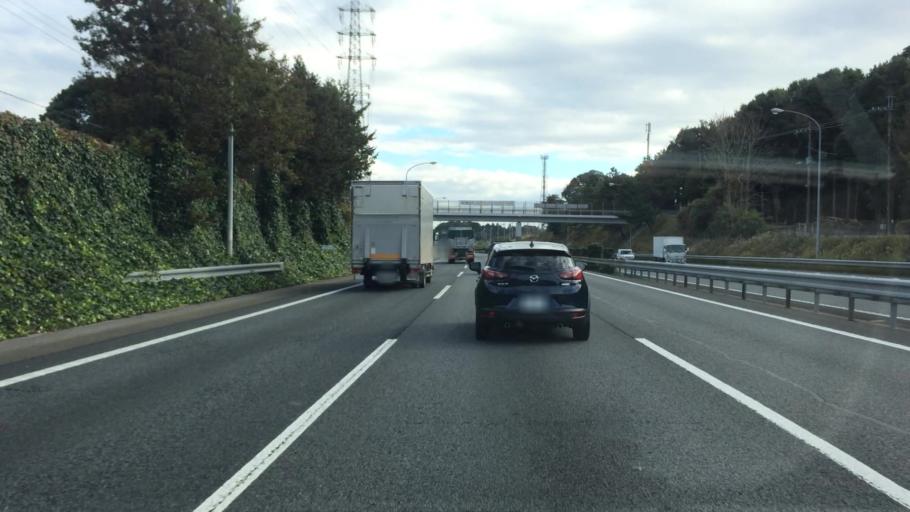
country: JP
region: Chiba
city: Sakura
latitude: 35.6827
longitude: 140.2113
